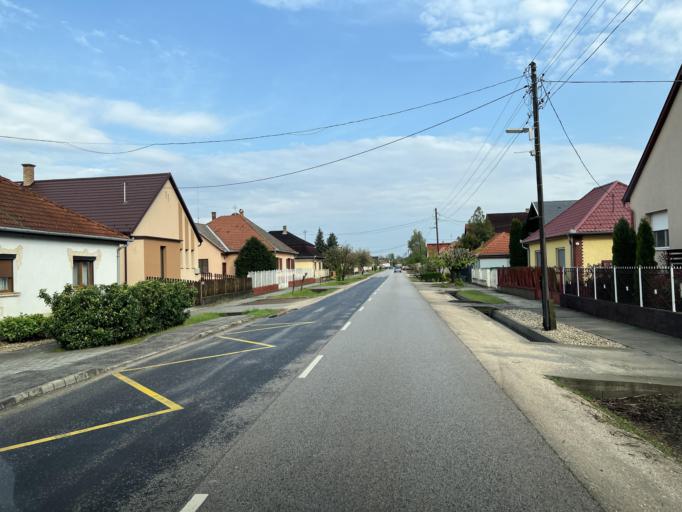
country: HU
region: Pest
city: Nyaregyhaza
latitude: 47.2283
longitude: 19.4523
